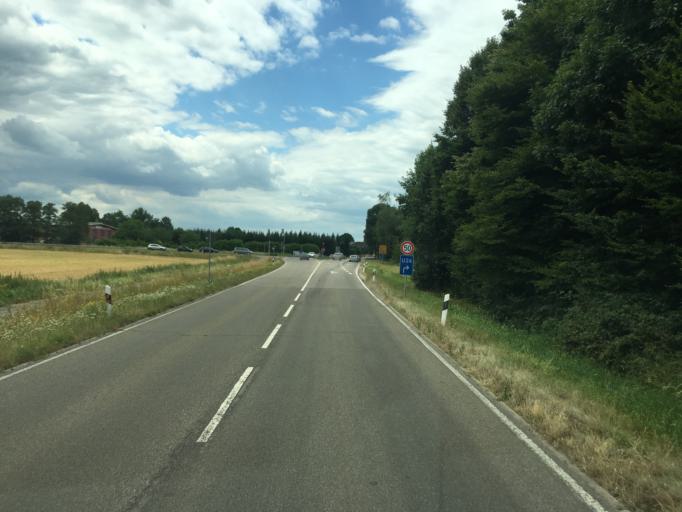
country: DE
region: Baden-Wuerttemberg
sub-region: Karlsruhe Region
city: Ottenhofen
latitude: 48.7218
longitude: 8.1252
